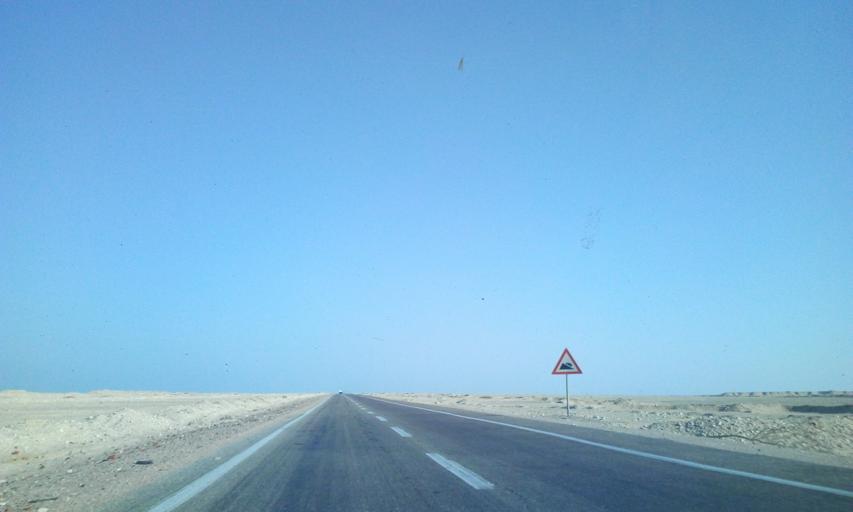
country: EG
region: As Suways
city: Ain Sukhna
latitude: 28.8409
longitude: 32.7040
